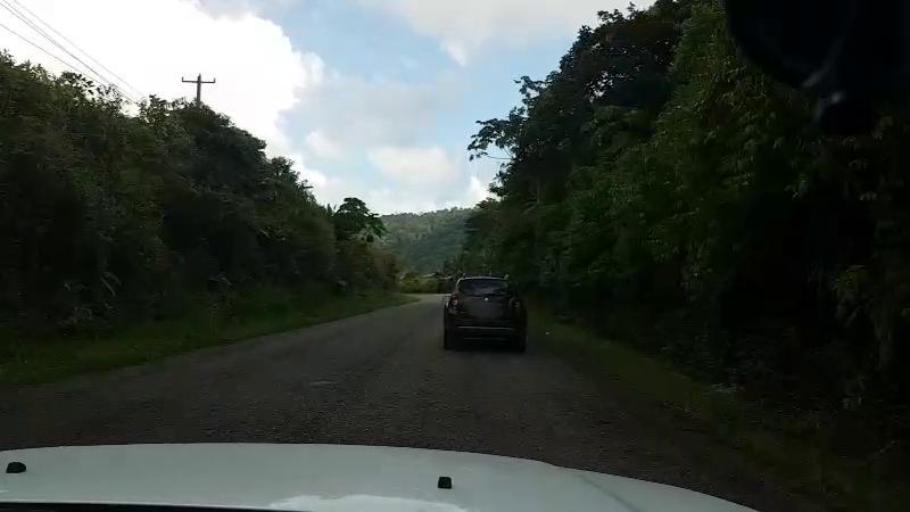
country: BZ
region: Stann Creek
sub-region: Dangriga
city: Dangriga
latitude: 17.0001
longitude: -88.4318
